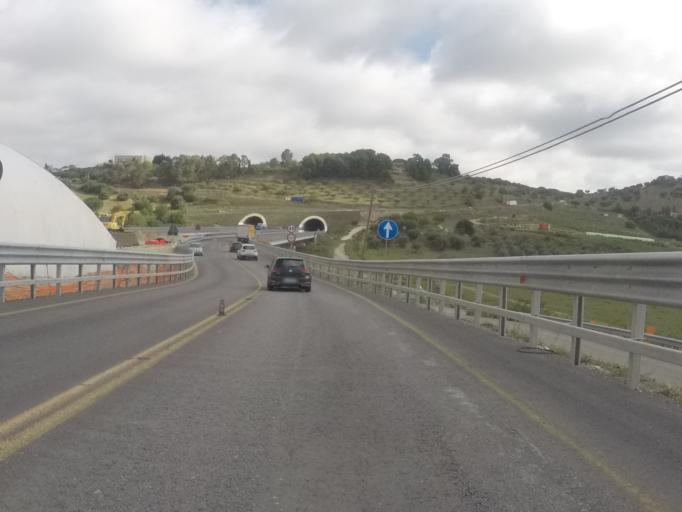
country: IT
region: Sicily
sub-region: Provincia di Caltanissetta
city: San Cataldo
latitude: 37.4573
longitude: 13.9934
